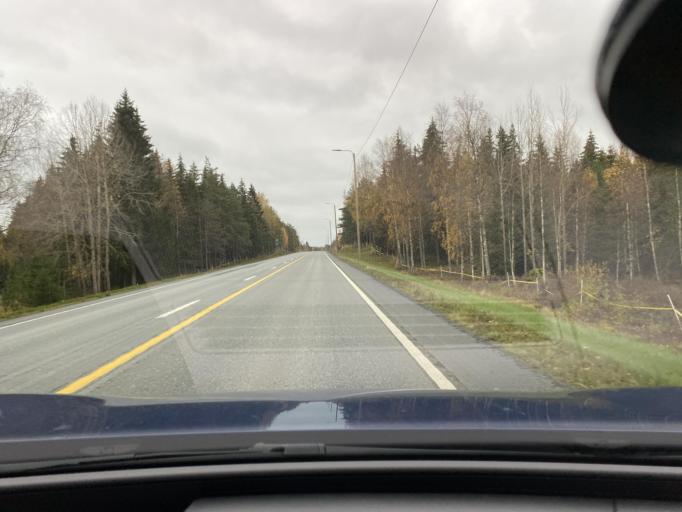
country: FI
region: Varsinais-Suomi
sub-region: Vakka-Suomi
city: Laitila
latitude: 60.9457
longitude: 21.6004
